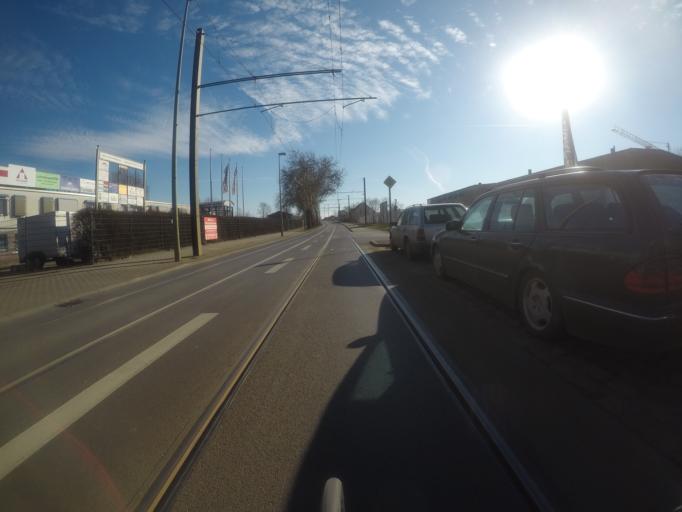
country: DE
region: Berlin
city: Kopenick Bezirk
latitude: 52.4303
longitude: 13.5718
